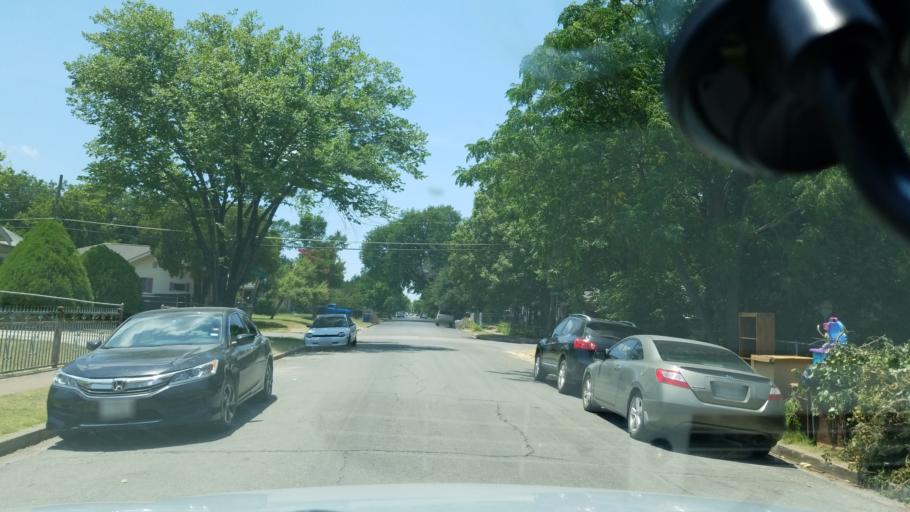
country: US
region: Texas
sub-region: Dallas County
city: Cockrell Hill
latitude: 32.7311
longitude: -96.8588
